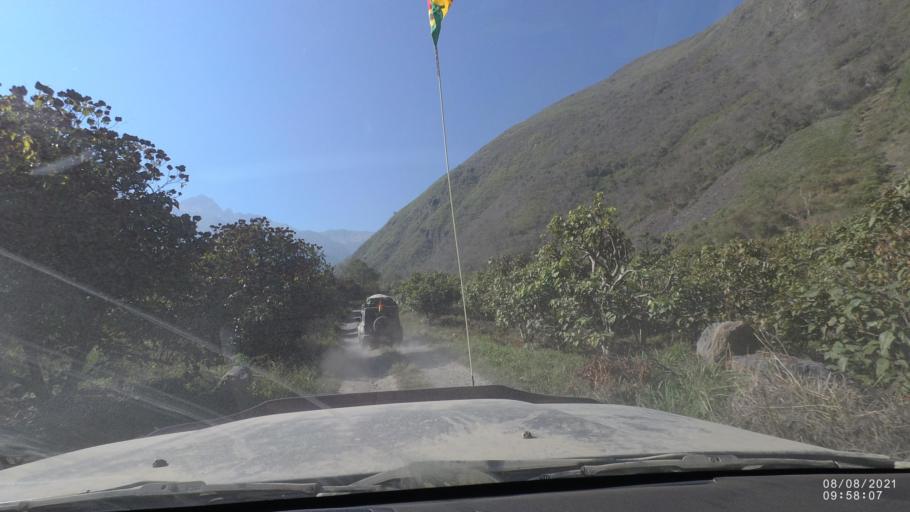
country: BO
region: La Paz
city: Quime
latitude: -16.6433
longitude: -66.7259
